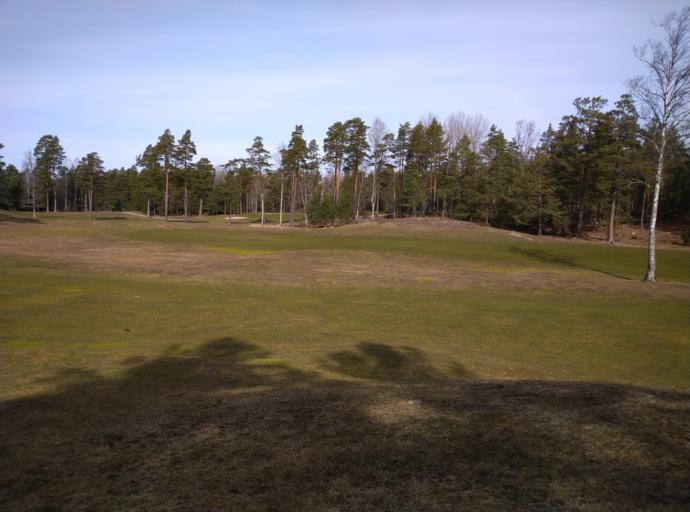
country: SE
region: Stockholm
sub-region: Nacka Kommun
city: Fisksatra
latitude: 59.2857
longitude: 18.2446
